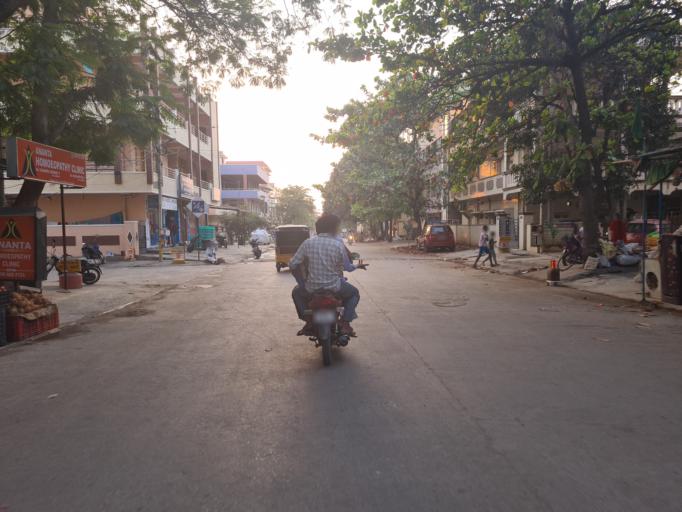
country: IN
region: Telangana
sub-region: Medak
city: Serilingampalle
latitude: 17.4778
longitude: 78.2857
